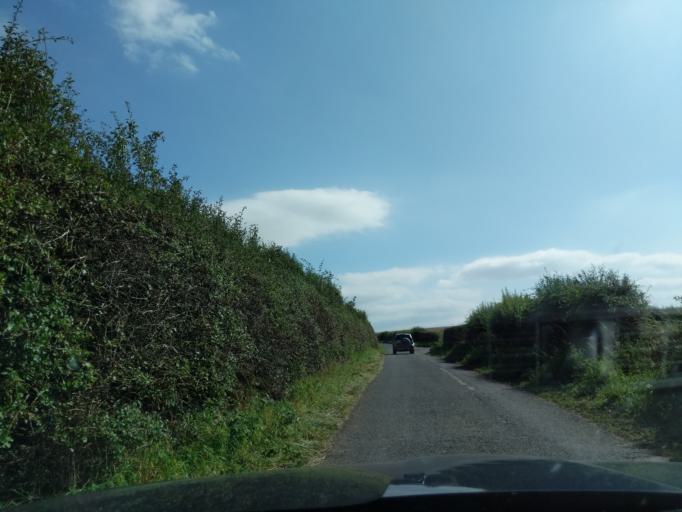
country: GB
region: England
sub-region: Northumberland
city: Ford
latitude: 55.6680
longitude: -2.1653
